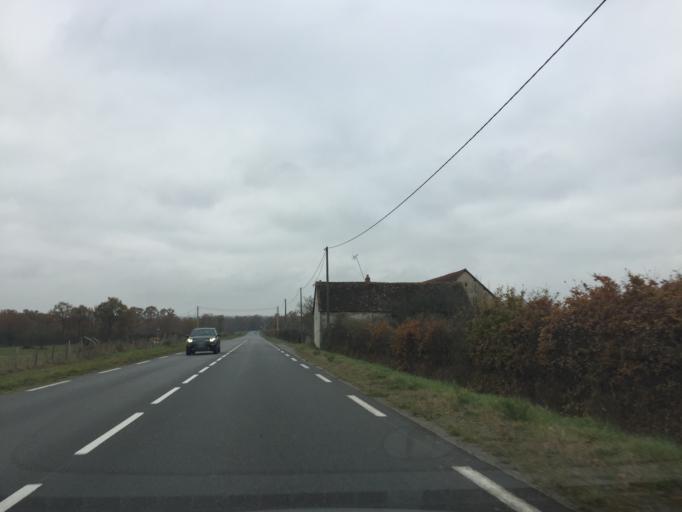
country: FR
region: Limousin
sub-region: Departement de la Creuse
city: Gouzon
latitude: 46.1683
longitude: 2.2190
